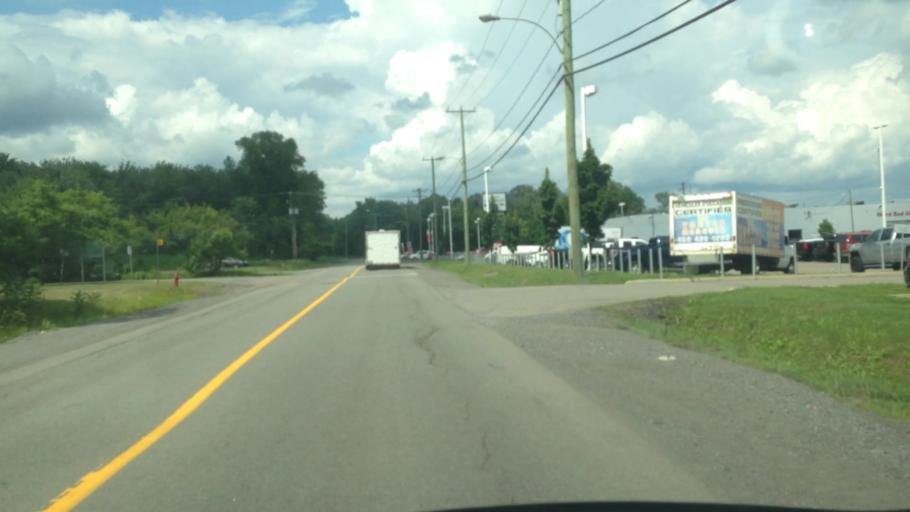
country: CA
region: Quebec
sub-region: Laurentides
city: Saint-Jerome
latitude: 45.7726
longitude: -74.0228
